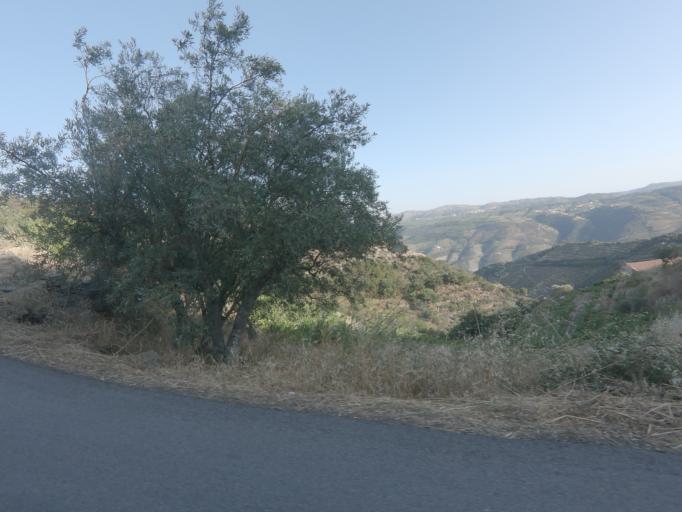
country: PT
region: Vila Real
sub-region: Sabrosa
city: Vilela
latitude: 41.1774
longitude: -7.6009
